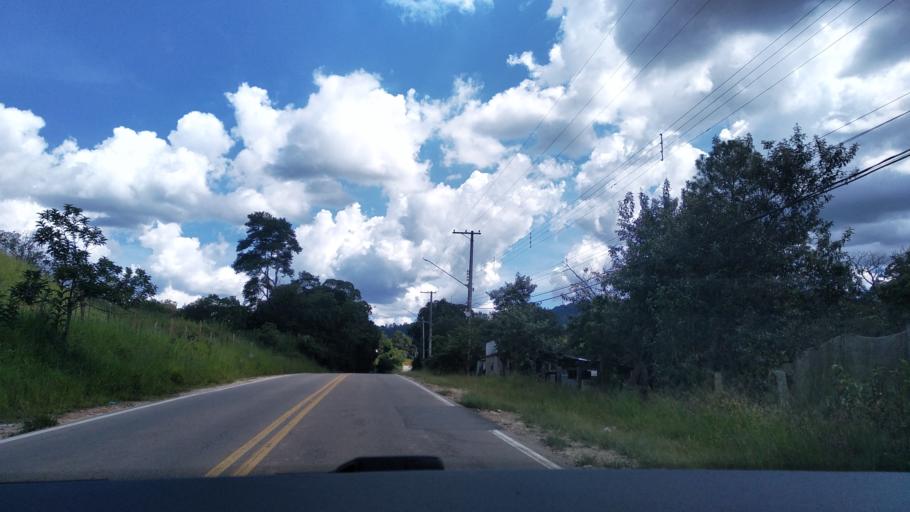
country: BR
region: Sao Paulo
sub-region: Varzea Paulista
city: Varzea Paulista
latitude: -23.2581
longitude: -46.8801
